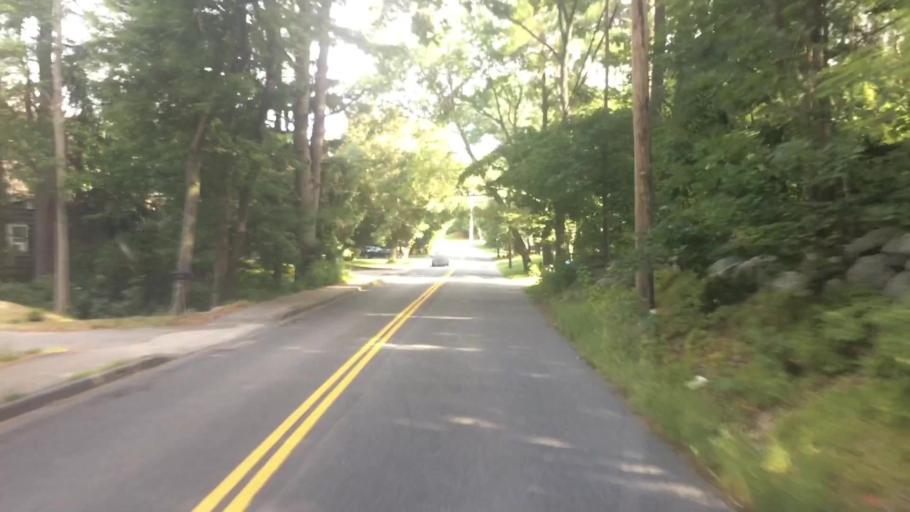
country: US
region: Massachusetts
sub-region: Middlesex County
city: Acton
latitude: 42.4713
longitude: -71.4587
